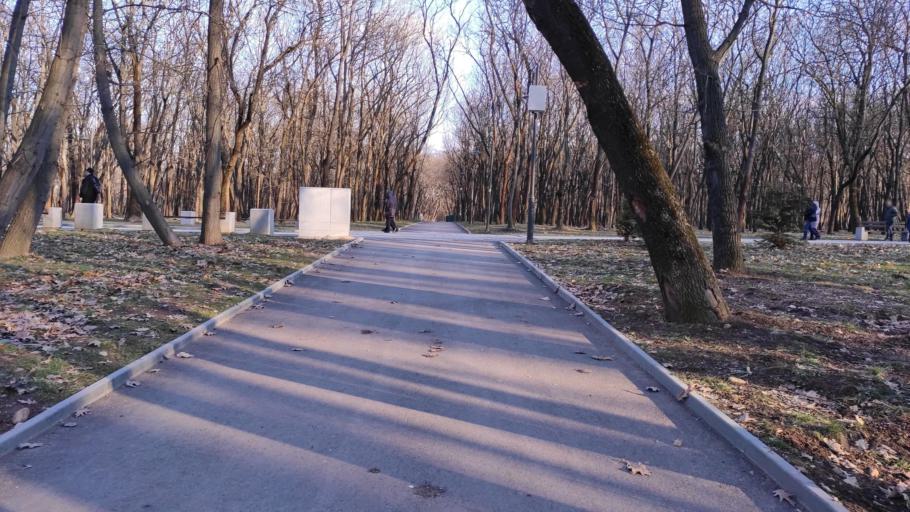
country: BG
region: Sofia-Capital
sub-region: Stolichna Obshtina
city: Sofia
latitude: 42.7114
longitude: 23.2778
